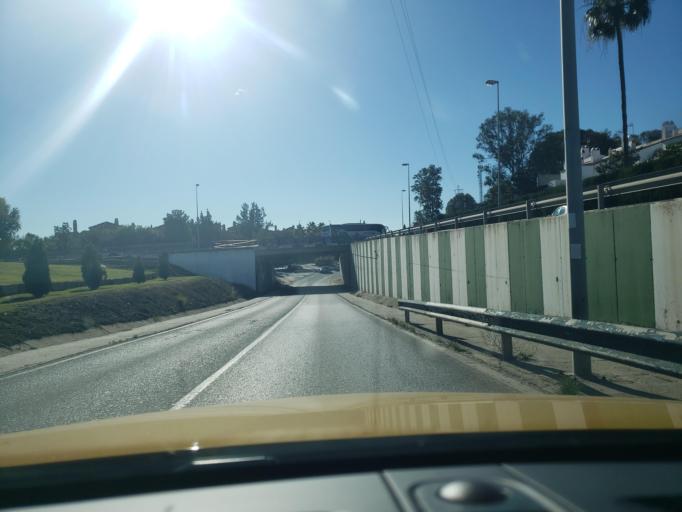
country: ES
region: Andalusia
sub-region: Provincia de Malaga
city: Benahavis
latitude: 36.4724
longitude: -5.0113
